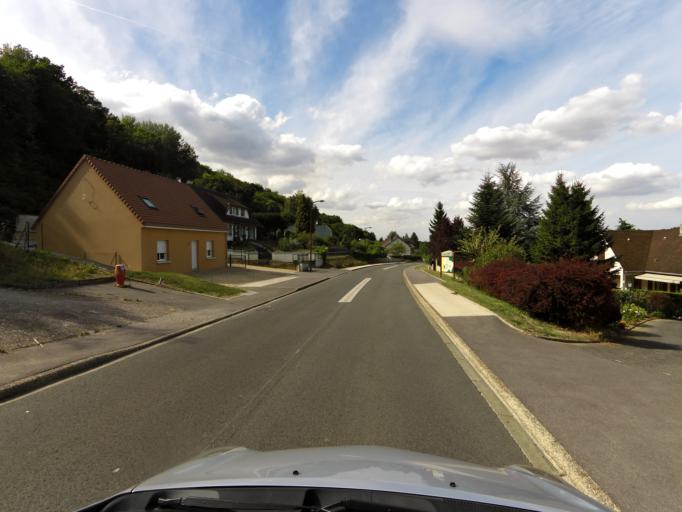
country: FR
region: Picardie
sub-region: Departement de l'Aisne
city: Bruyeres-et-Montberault
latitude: 49.5184
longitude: 3.6668
